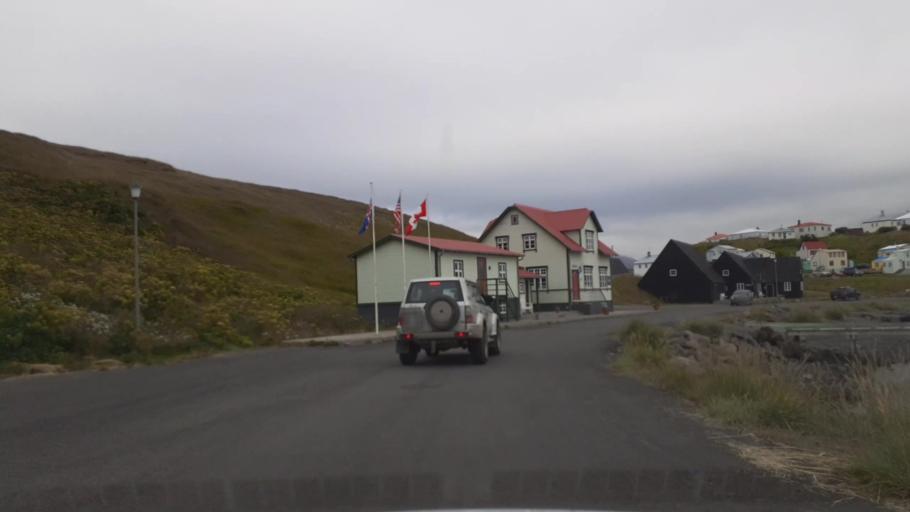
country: IS
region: Northwest
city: Saudarkrokur
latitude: 65.8991
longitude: -19.4211
